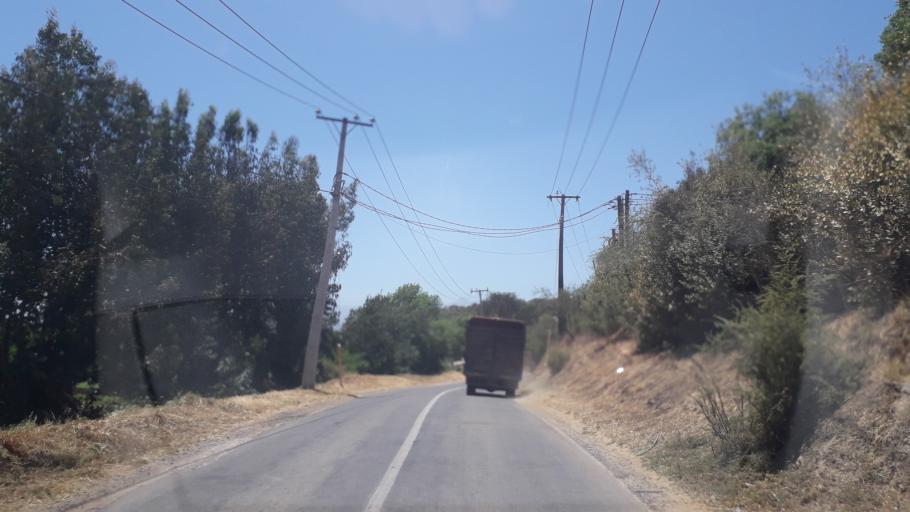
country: CL
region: Valparaiso
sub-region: Provincia de Quillota
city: Quillota
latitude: -32.9344
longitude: -71.2644
